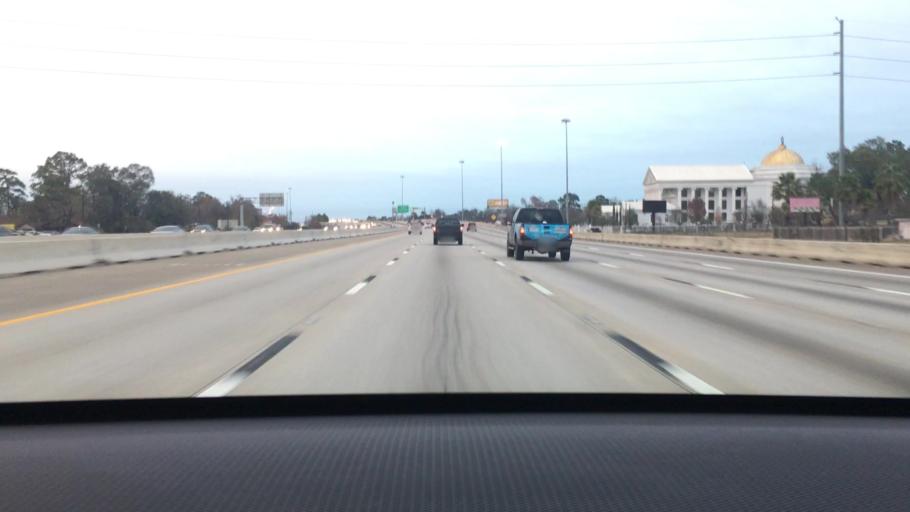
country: US
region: Texas
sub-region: Harris County
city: Houston
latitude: 29.8333
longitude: -95.3342
